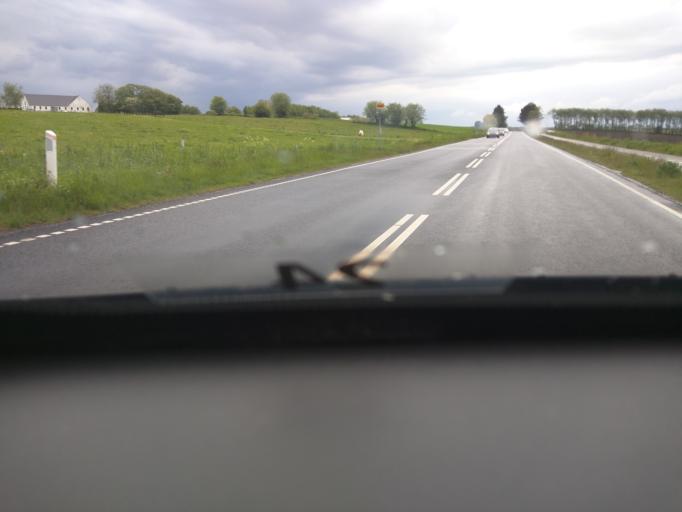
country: DK
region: Central Jutland
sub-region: Viborg Kommune
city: Viborg
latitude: 56.4641
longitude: 9.4997
